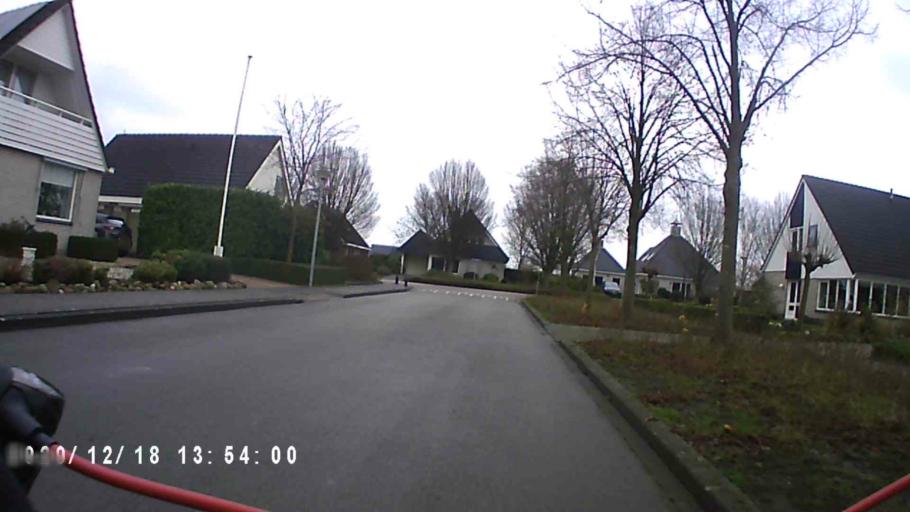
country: NL
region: Groningen
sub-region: Gemeente Bedum
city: Bedum
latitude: 53.2986
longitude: 6.6139
